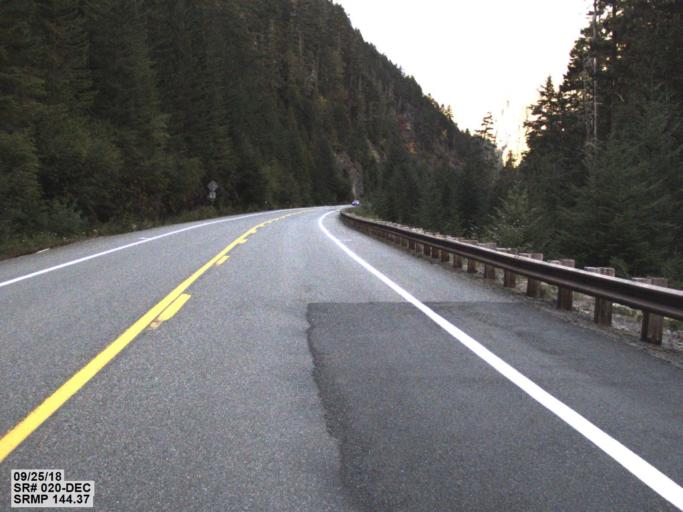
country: US
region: Washington
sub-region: Snohomish County
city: Darrington
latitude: 48.6726
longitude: -120.8778
